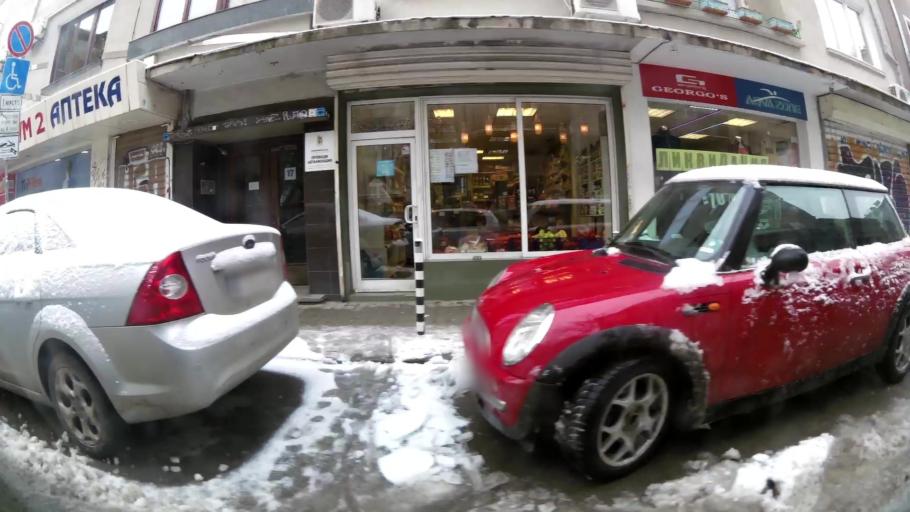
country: BG
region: Sofia-Capital
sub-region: Stolichna Obshtina
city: Sofia
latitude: 42.6915
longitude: 23.3300
